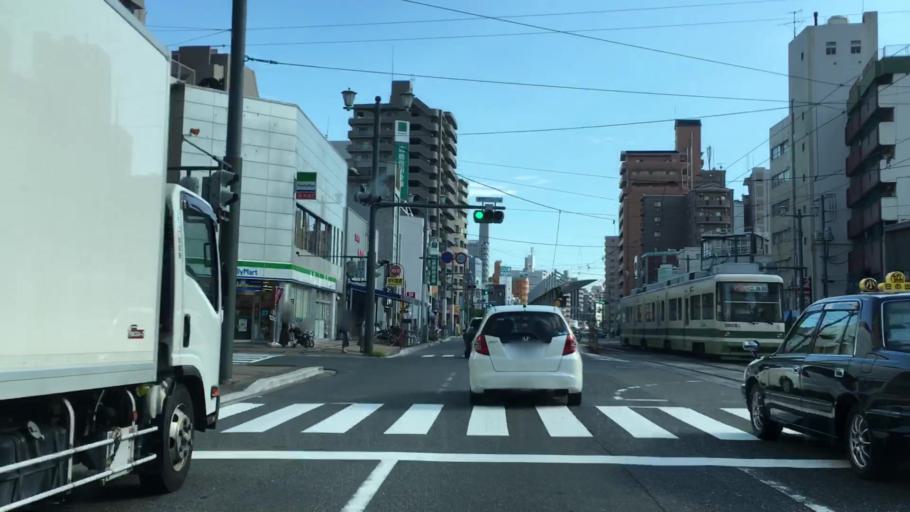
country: JP
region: Hiroshima
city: Hiroshima-shi
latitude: 34.3949
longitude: 132.4464
